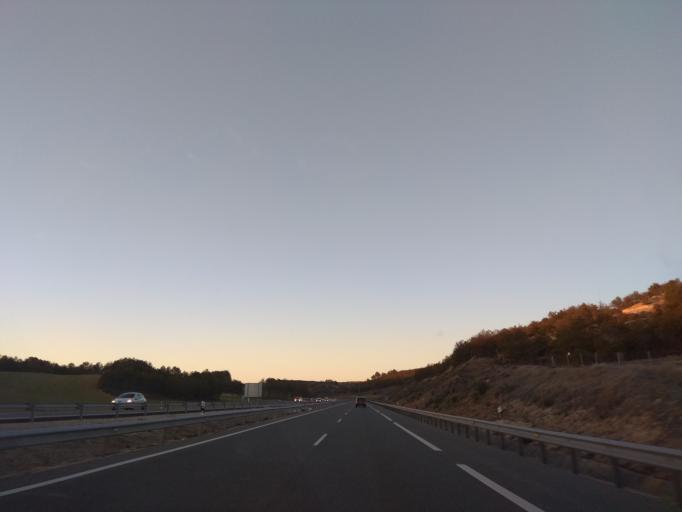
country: ES
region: Castille and Leon
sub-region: Provincia de Burgos
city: Bahabon de Esgueva
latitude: 41.8750
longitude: -3.7315
